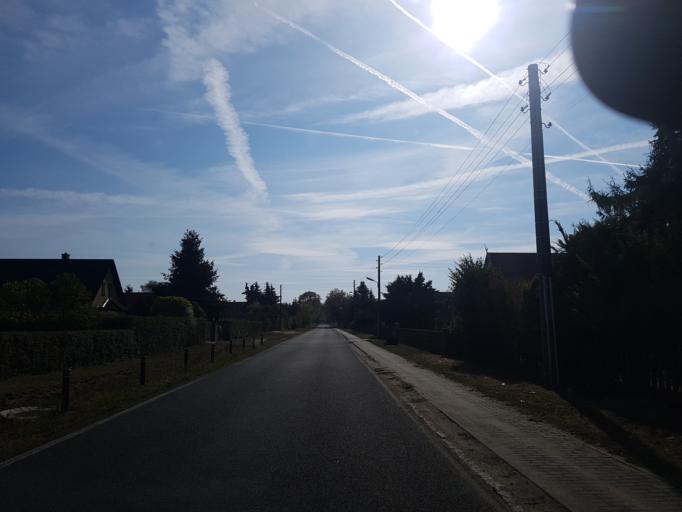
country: DE
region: Brandenburg
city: Lebusa
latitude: 51.8295
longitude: 13.3903
